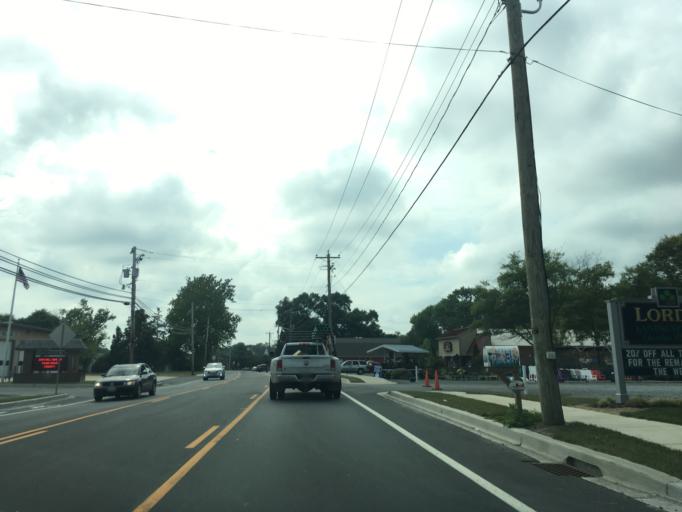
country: US
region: Delaware
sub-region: Sussex County
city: Ocean View
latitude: 38.5475
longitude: -75.1098
